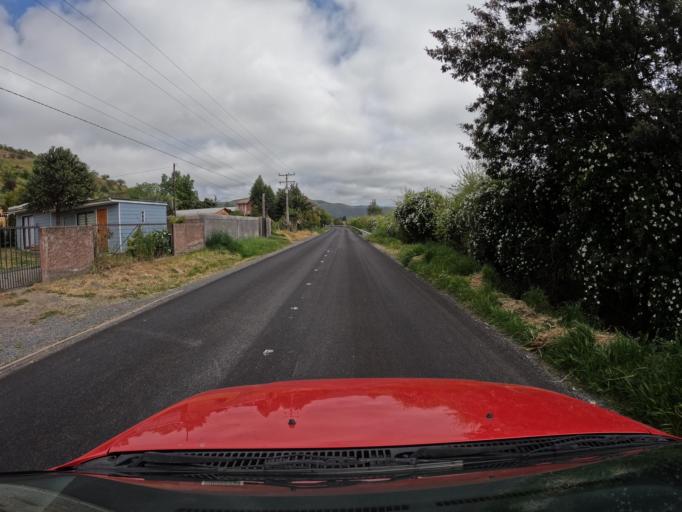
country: CL
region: O'Higgins
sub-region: Provincia de Colchagua
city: Santa Cruz
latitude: -34.6604
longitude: -71.4018
